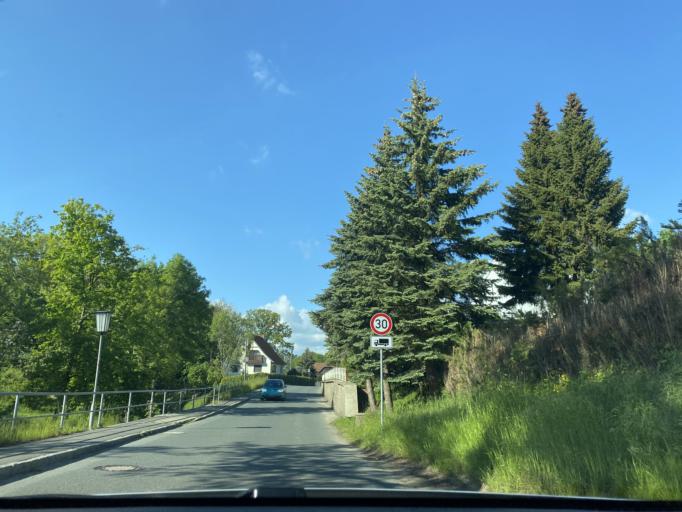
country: DE
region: Saxony
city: Markersdorf
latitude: 51.1336
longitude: 14.8784
